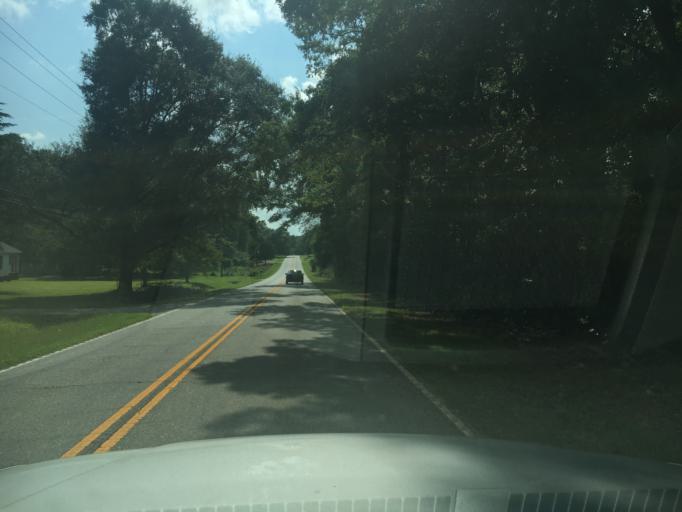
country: US
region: South Carolina
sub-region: Anderson County
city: Belton
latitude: 34.5313
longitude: -82.4736
